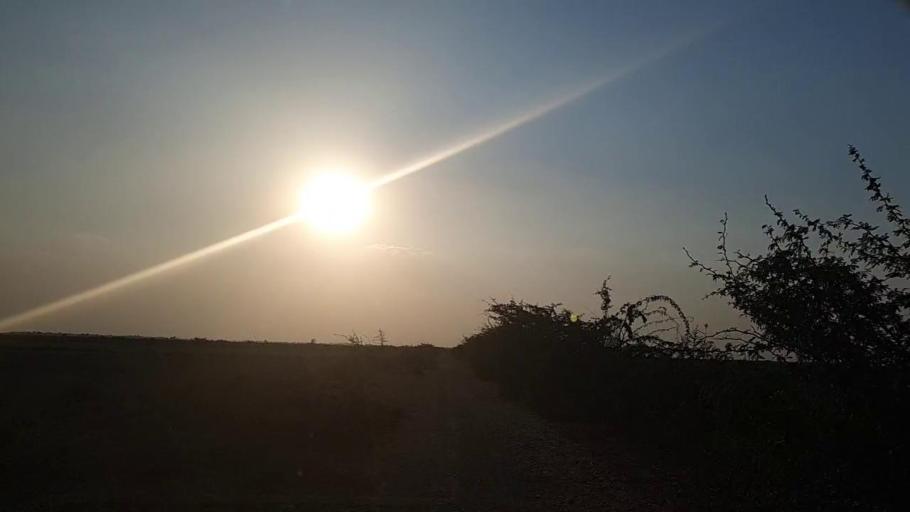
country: PK
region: Sindh
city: Jati
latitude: 24.4802
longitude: 68.4121
